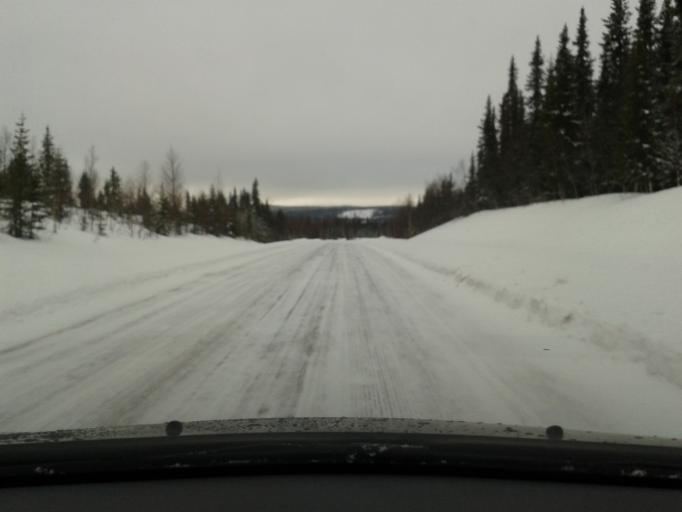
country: SE
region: Vaesterbotten
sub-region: Vilhelmina Kommun
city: Sjoberg
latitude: 65.0383
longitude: 15.9045
